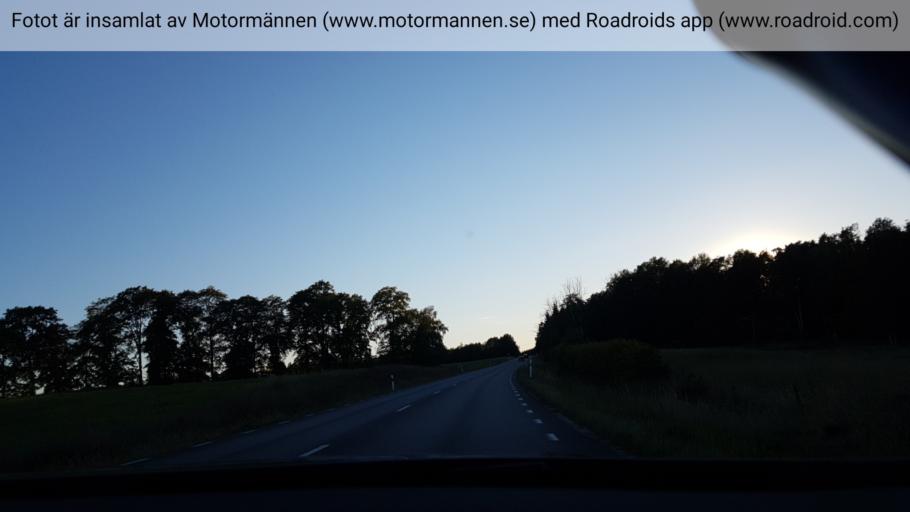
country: SE
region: Vaestra Goetaland
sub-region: Tibro Kommun
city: Tibro
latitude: 58.3462
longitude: 14.1188
